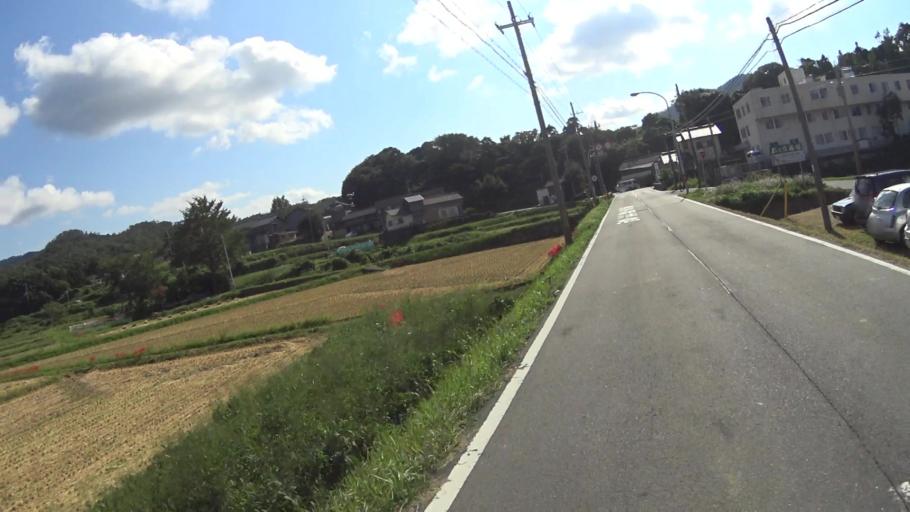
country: JP
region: Kyoto
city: Miyazu
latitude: 35.7550
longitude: 135.1727
